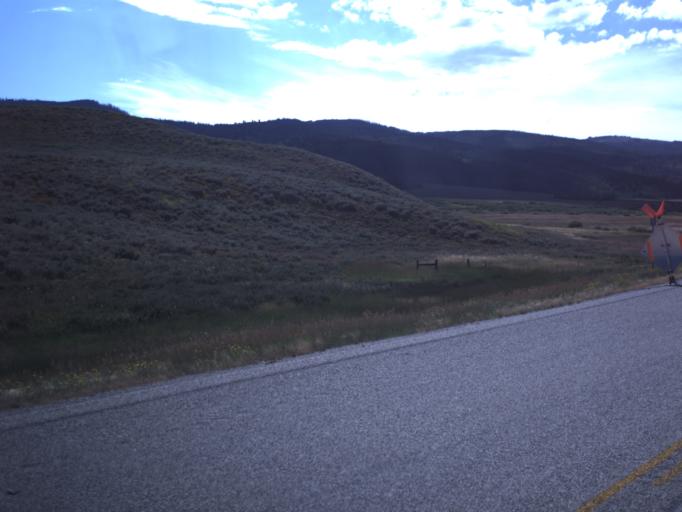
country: US
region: Utah
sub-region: Wasatch County
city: Heber
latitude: 40.2785
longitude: -111.2184
